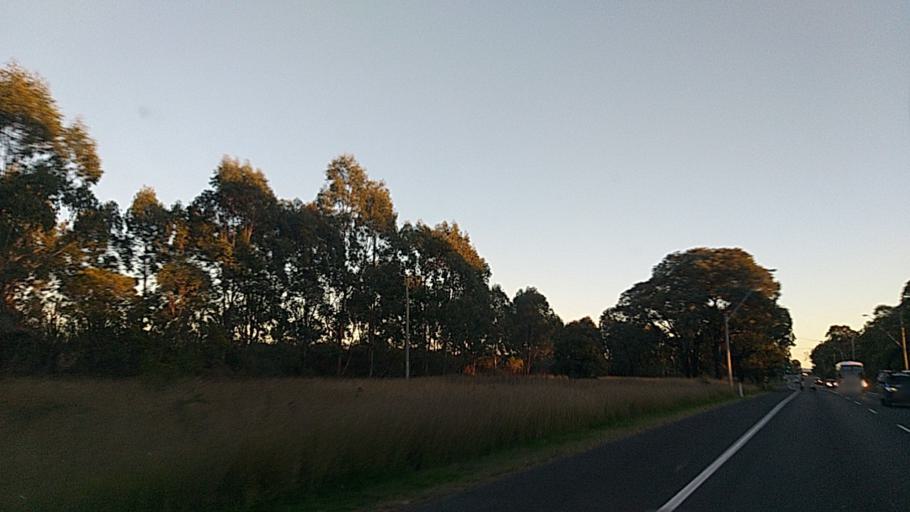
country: AU
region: New South Wales
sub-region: Hawkesbury
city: South Windsor
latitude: -33.6716
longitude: 150.8065
